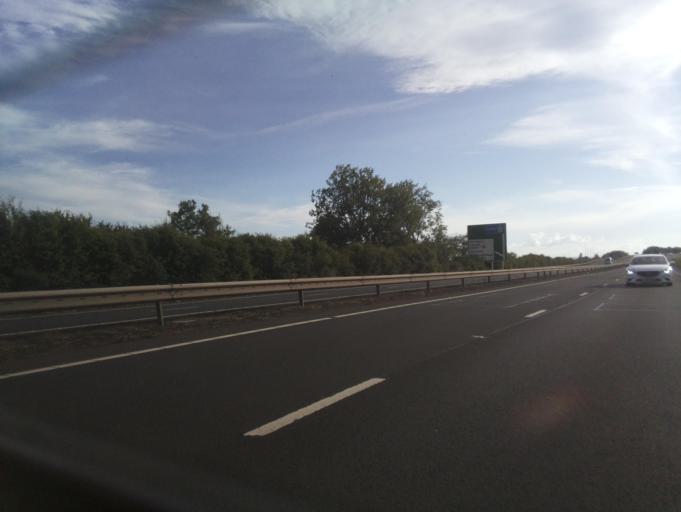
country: GB
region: Scotland
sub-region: Falkirk
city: Airth
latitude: 56.0574
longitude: -3.7504
